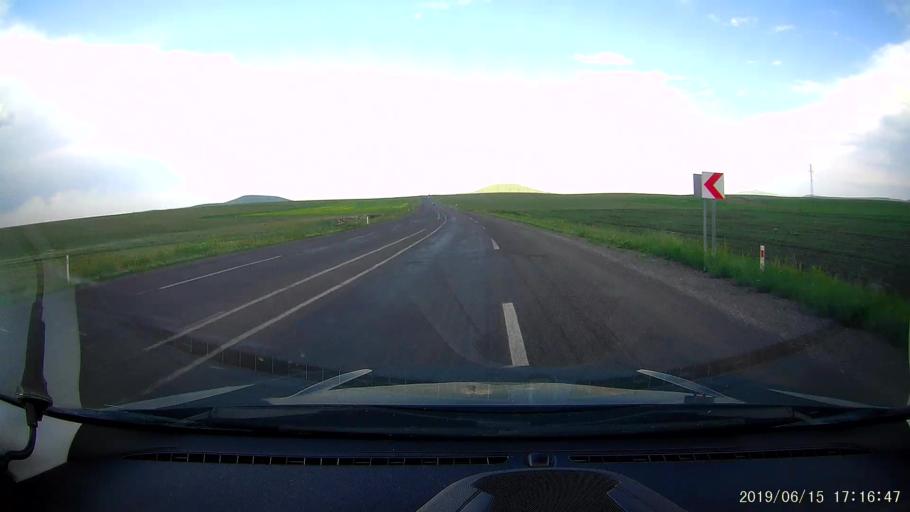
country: TR
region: Kars
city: Kars
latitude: 40.6144
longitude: 43.2247
